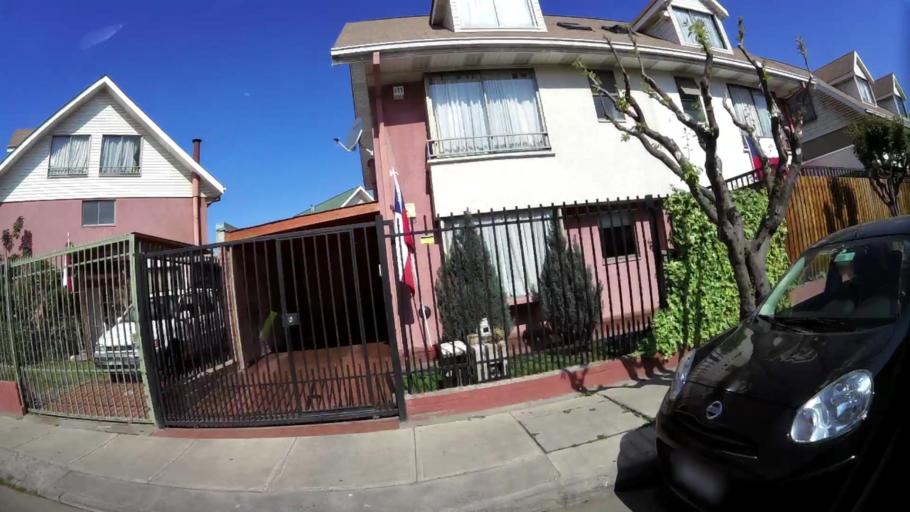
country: CL
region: Santiago Metropolitan
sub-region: Provincia de Santiago
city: Lo Prado
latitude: -33.4810
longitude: -70.7594
